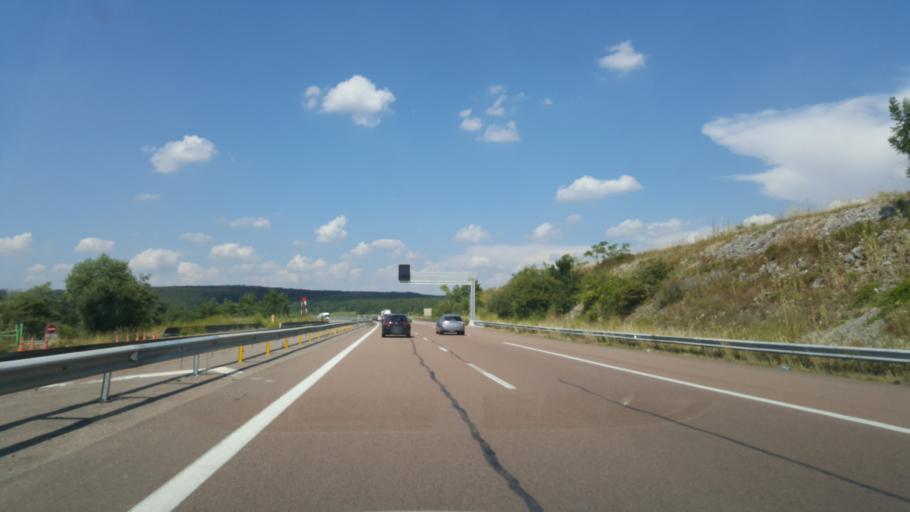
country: FR
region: Bourgogne
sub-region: Departement de la Cote-d'Or
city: Savigny-les-Beaune
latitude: 47.1609
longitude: 4.6979
